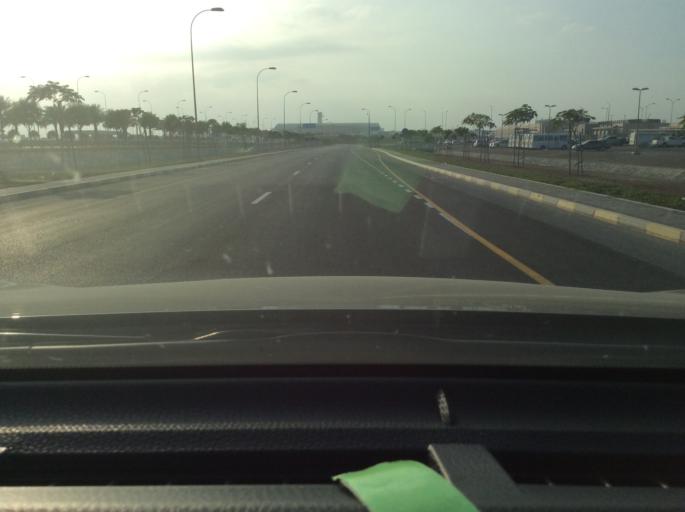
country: OM
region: Muhafazat Masqat
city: Bawshar
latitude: 23.6028
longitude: 58.3033
